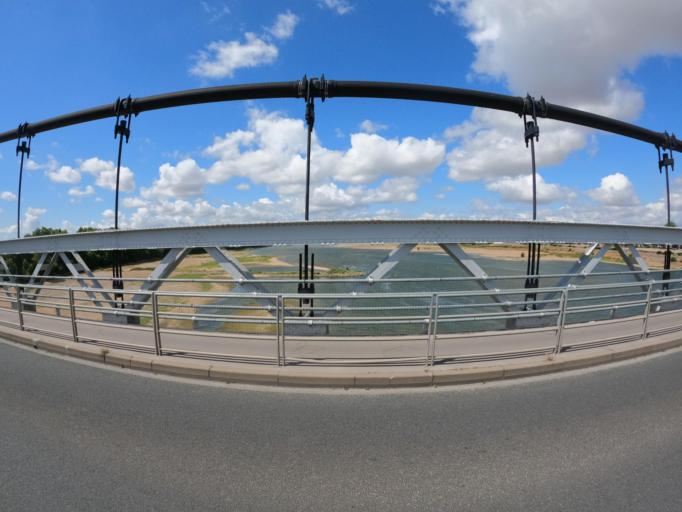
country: FR
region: Pays de la Loire
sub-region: Departement de la Loire-Atlantique
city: Ancenis
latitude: 47.3620
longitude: -1.1770
